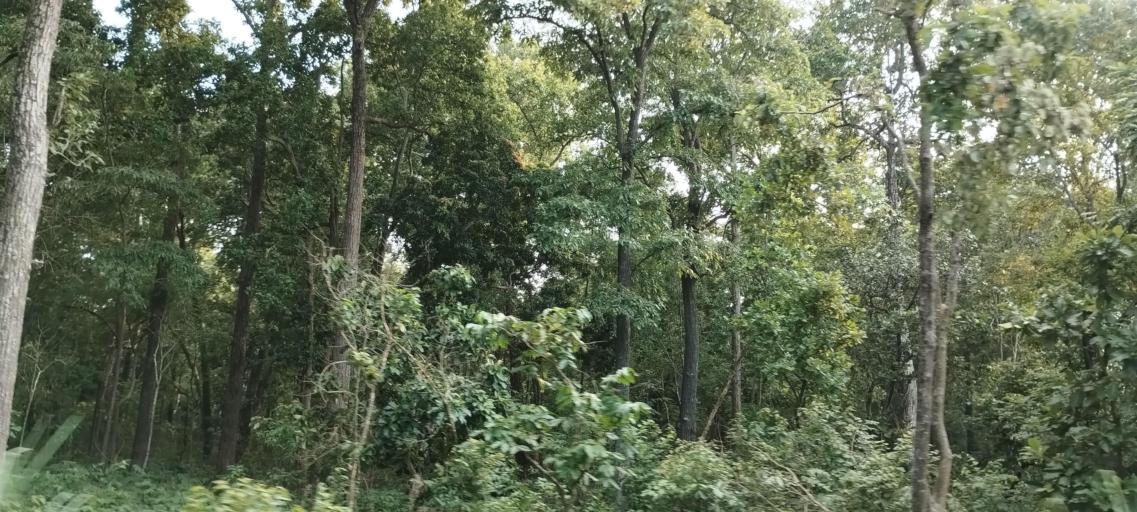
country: NP
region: Mid Western
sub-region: Bheri Zone
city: Bardiya
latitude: 28.4294
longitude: 81.3703
